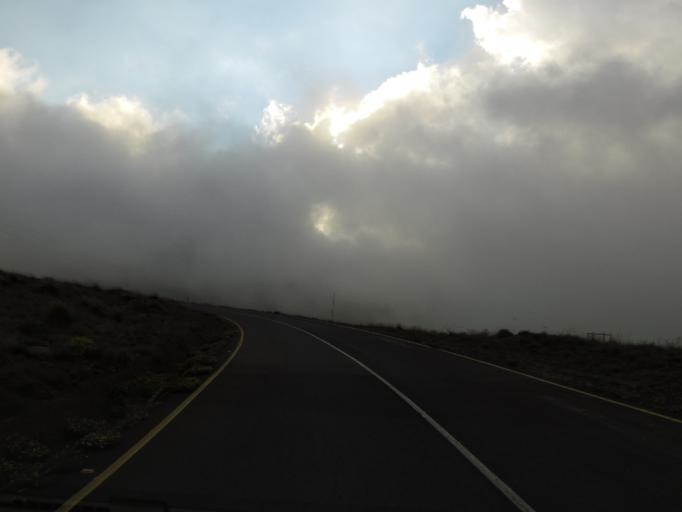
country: LS
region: Butha-Buthe
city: Butha-Buthe
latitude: -29.0659
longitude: 28.4148
